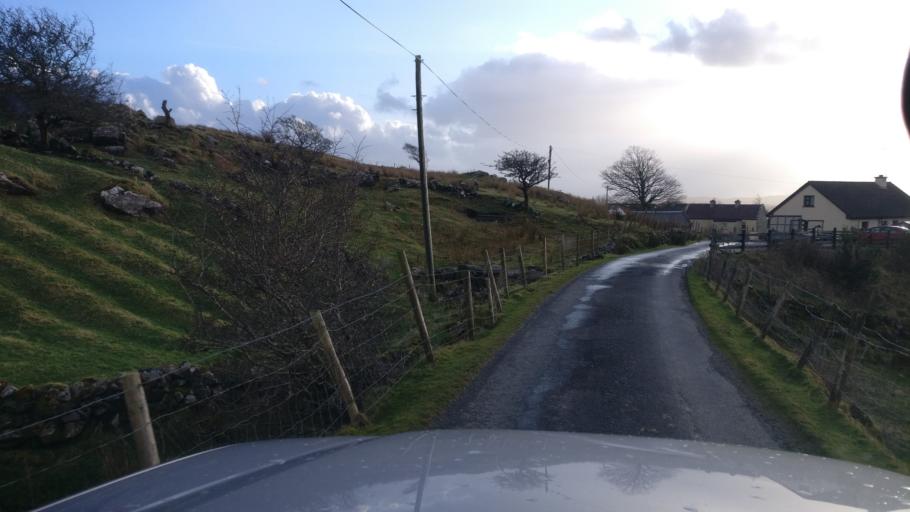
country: IE
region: Connaught
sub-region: County Galway
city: Clifden
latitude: 53.4756
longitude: -9.7261
